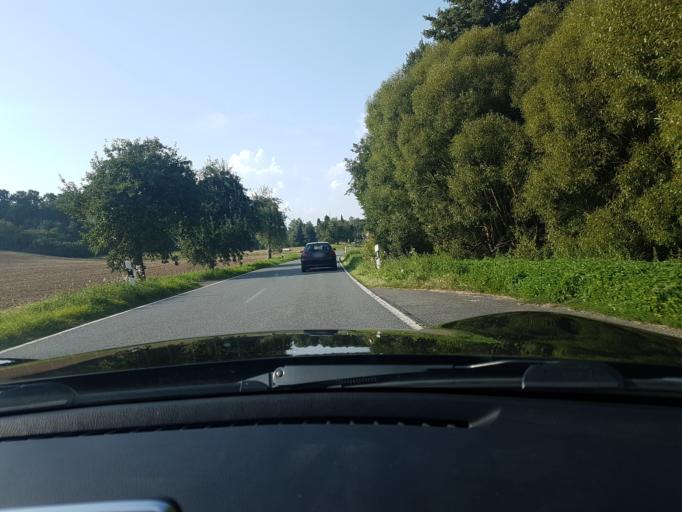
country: DE
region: Baden-Wuerttemberg
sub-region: Karlsruhe Region
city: Seckach
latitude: 49.4483
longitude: 9.3687
